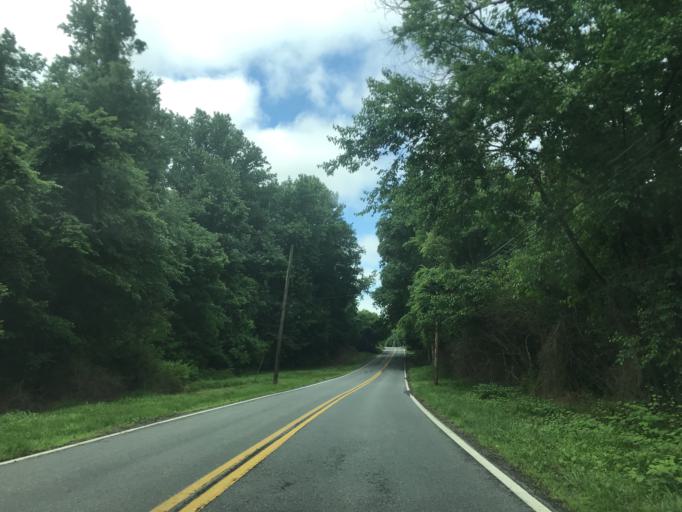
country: US
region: Maryland
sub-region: Caroline County
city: Ridgely
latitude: 38.8911
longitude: -75.9601
